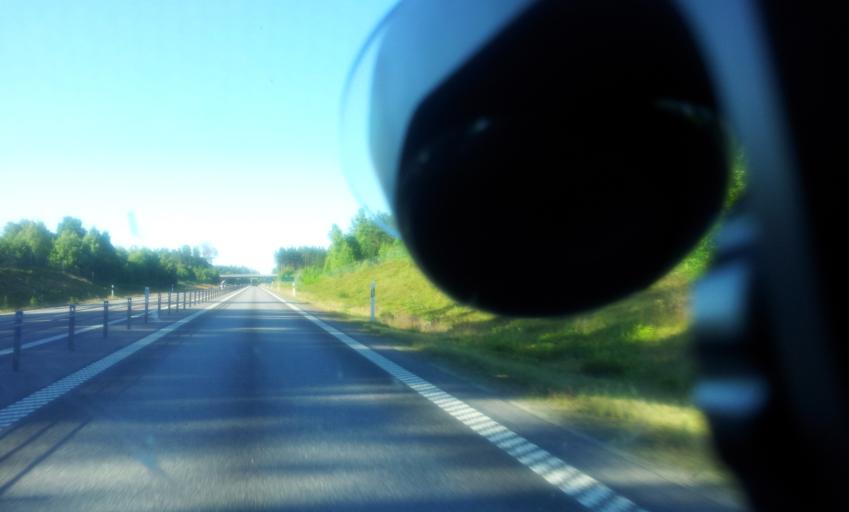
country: SE
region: Kalmar
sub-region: Torsas Kommun
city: Torsas
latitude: 56.5167
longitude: 16.0856
